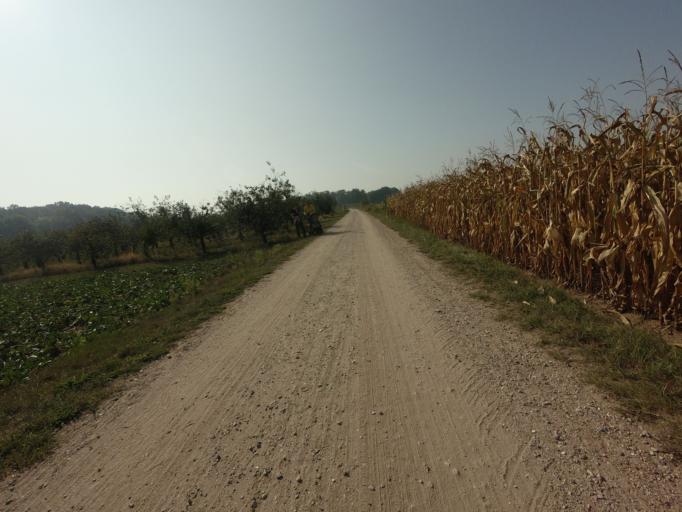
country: NL
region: Limburg
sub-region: Gemeente Beesel
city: Beesel
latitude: 51.2746
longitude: 6.0379
